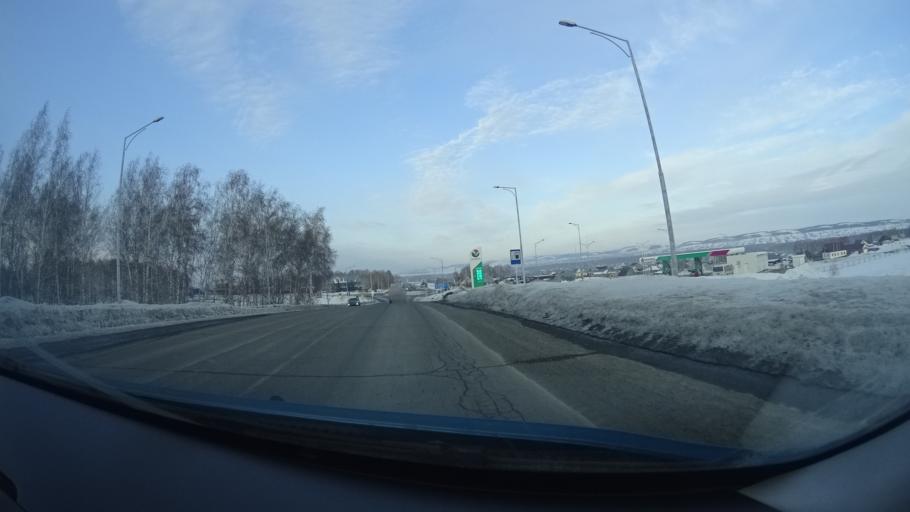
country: RU
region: Bashkortostan
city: Abzakovo
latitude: 53.3221
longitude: 58.5034
